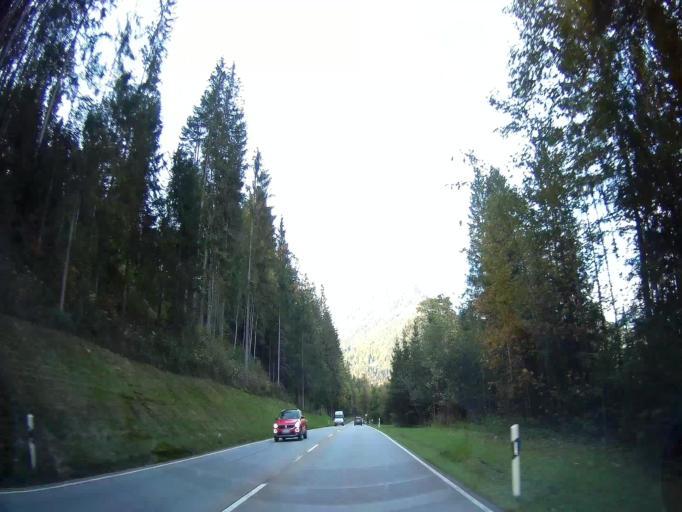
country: DE
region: Bavaria
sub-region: Upper Bavaria
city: Bischofswiesen
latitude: 47.6333
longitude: 12.9609
